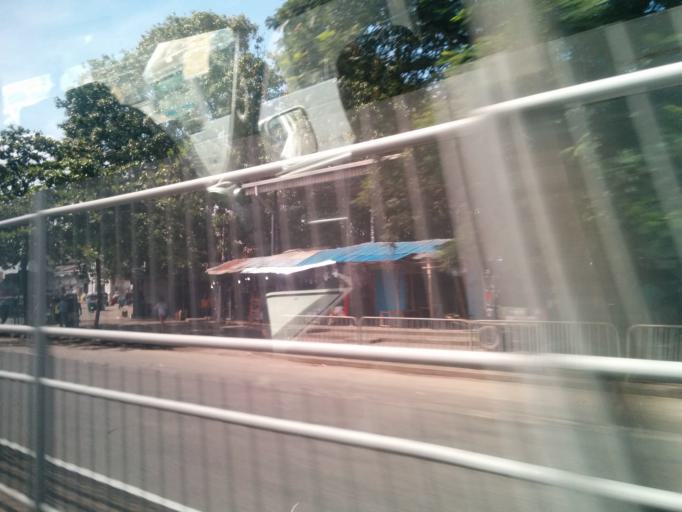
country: LK
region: Western
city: Colombo
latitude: 6.9341
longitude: 79.8488
